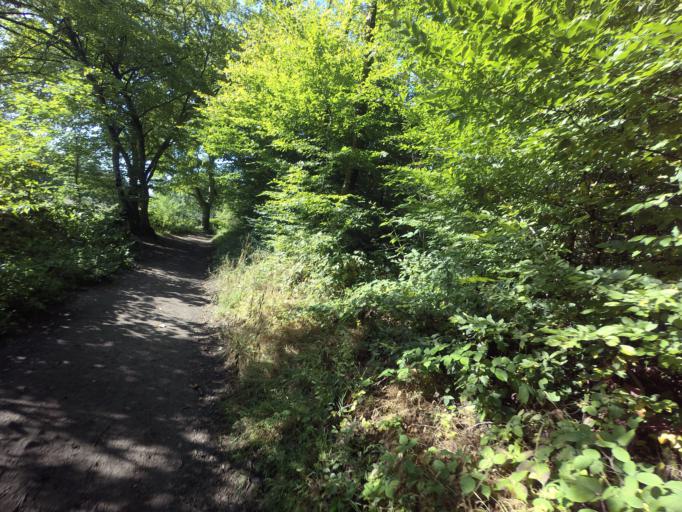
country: DE
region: North Rhine-Westphalia
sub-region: Regierungsbezirk Koln
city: Wurselen
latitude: 50.8151
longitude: 6.1032
